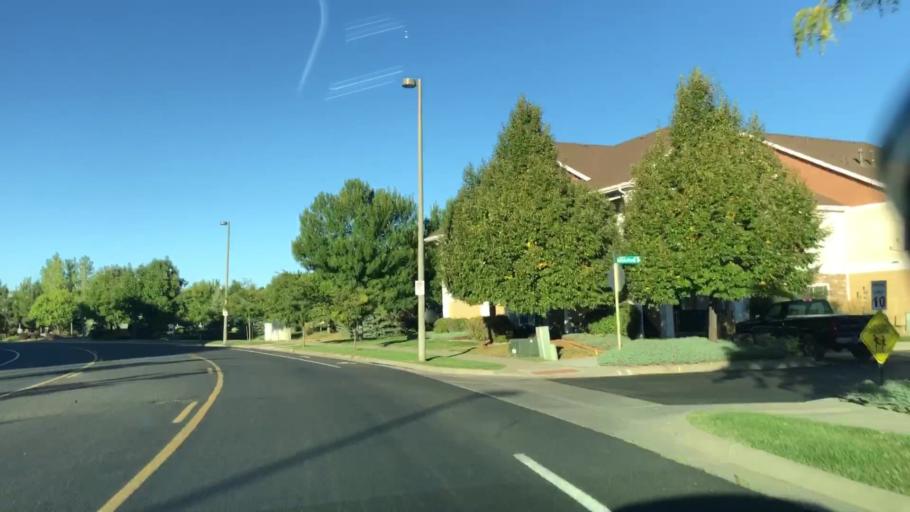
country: US
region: Colorado
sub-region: Larimer County
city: Loveland
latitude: 40.4127
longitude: -105.0097
